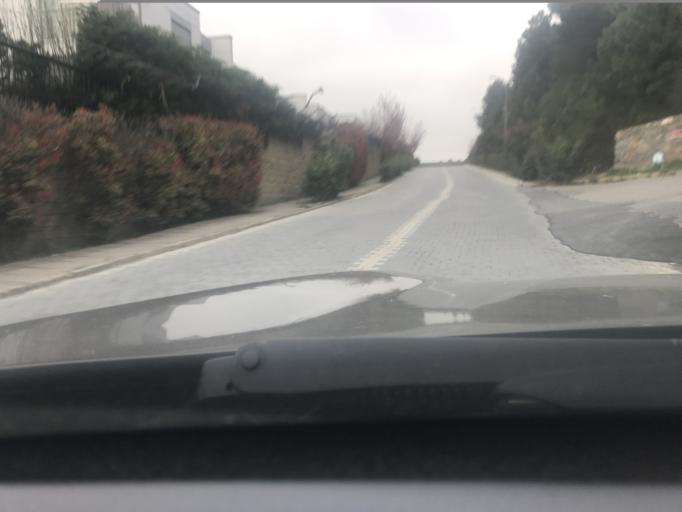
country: TR
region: Istanbul
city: Umraniye
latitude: 41.0406
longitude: 29.1581
